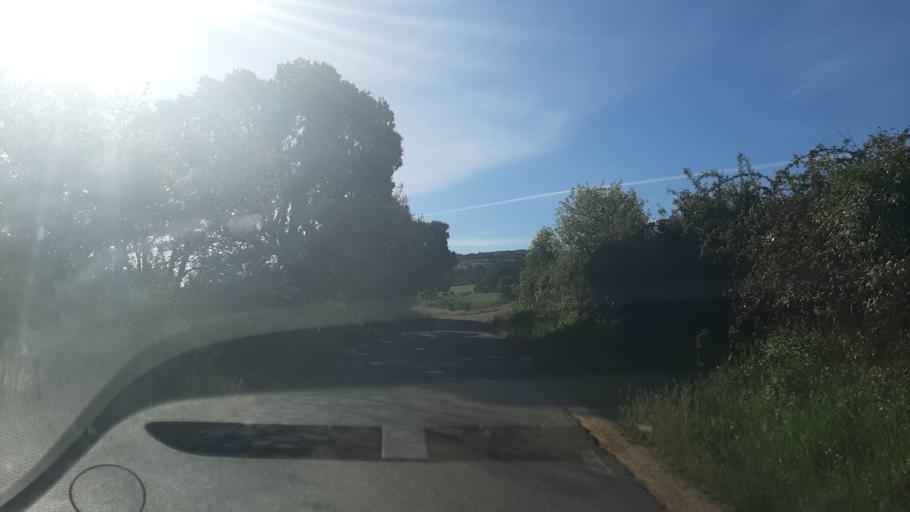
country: ES
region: Castille and Leon
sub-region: Provincia de Salamanca
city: Guijo de Avila
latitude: 40.5349
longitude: -5.6502
